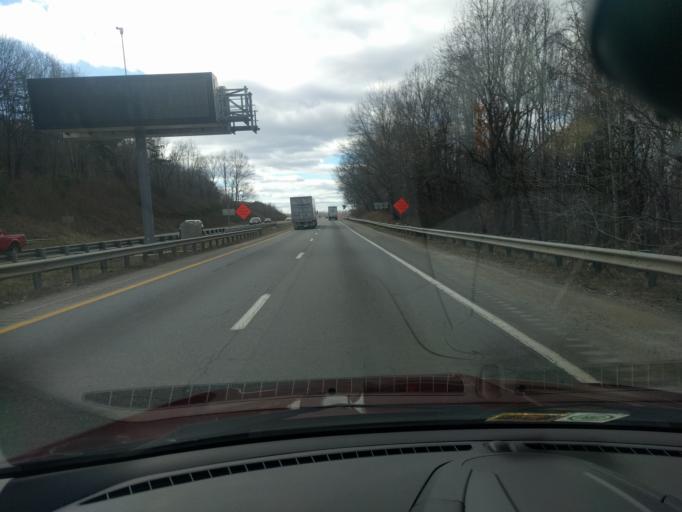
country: US
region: Virginia
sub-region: City of Lynchburg
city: Lynchburg
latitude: 37.3771
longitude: -79.1365
